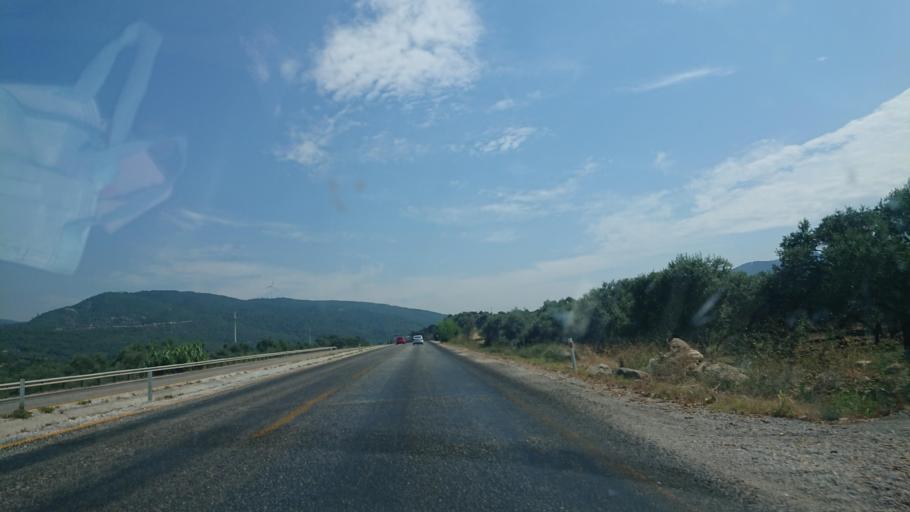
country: TR
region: Izmir
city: Dagkizilca
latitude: 38.3253
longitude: 27.4153
